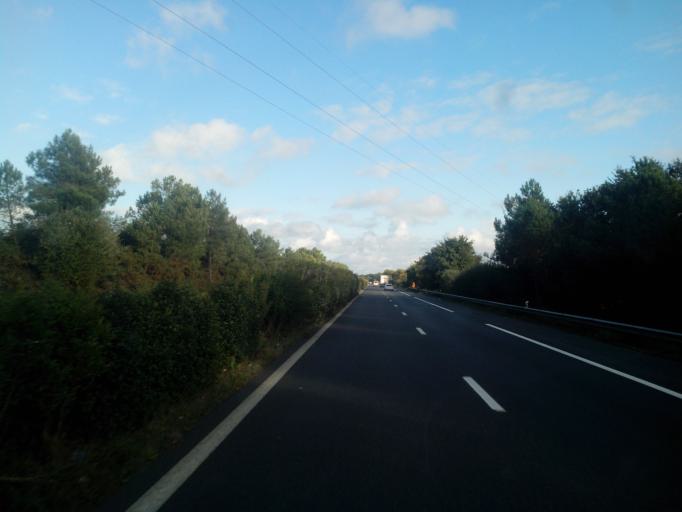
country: FR
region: Pays de la Loire
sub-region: Departement de la Loire-Atlantique
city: La Chapelle-des-Marais
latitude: 47.4921
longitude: -2.2392
